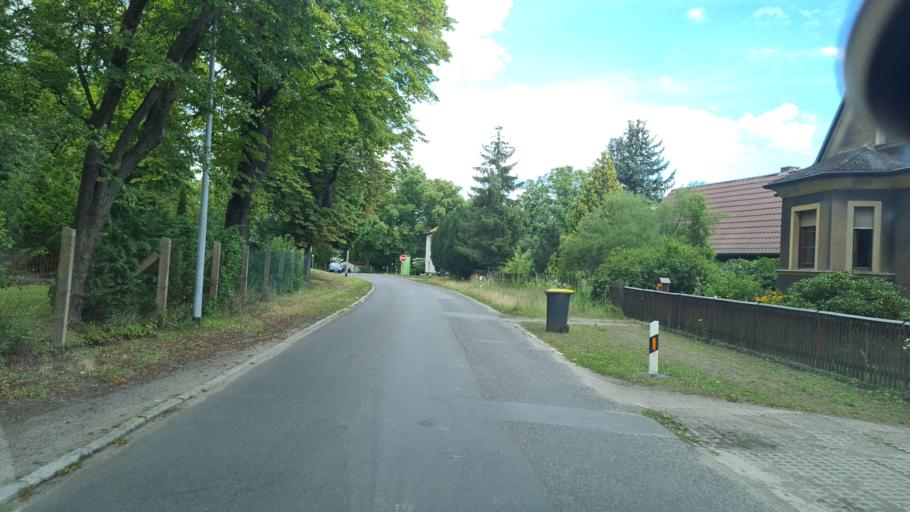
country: DE
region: Brandenburg
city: Drebkau
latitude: 51.6523
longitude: 14.2216
